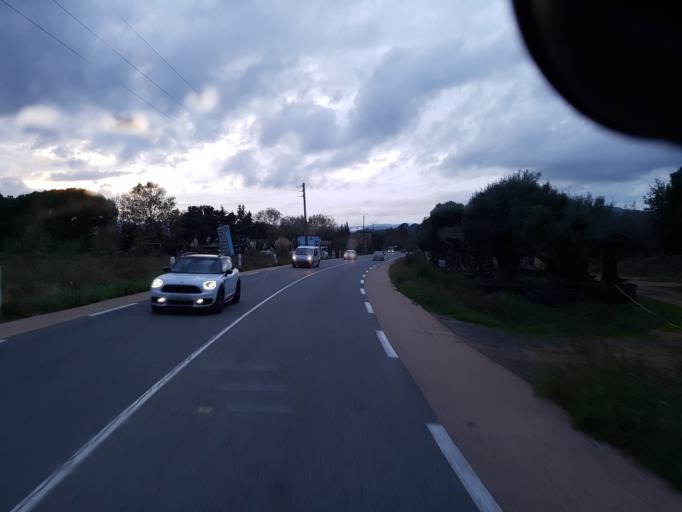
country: FR
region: Provence-Alpes-Cote d'Azur
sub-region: Departement du Var
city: Grimaud
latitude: 43.2696
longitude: 6.5479
